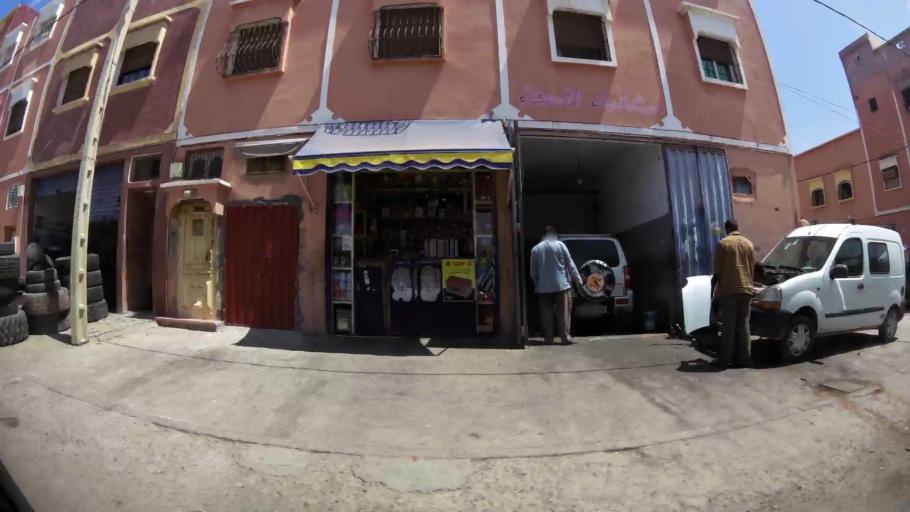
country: MA
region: Souss-Massa-Draa
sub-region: Inezgane-Ait Mellou
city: Inezgane
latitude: 30.3274
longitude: -9.4954
